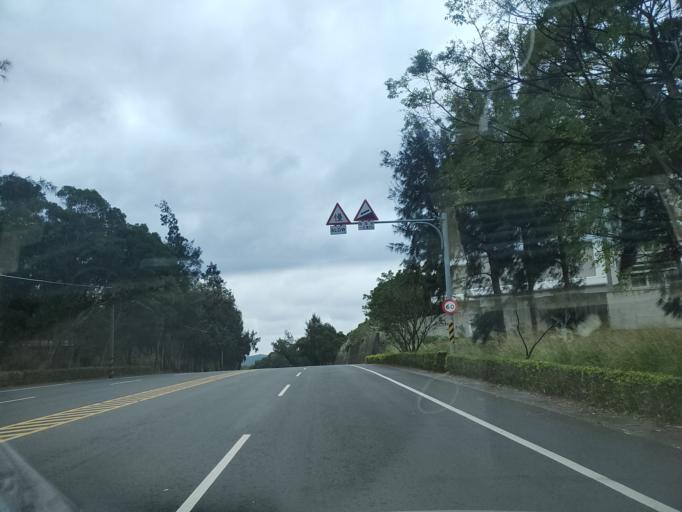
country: TW
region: Taiwan
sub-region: Miaoli
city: Miaoli
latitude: 24.5195
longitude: 120.7893
